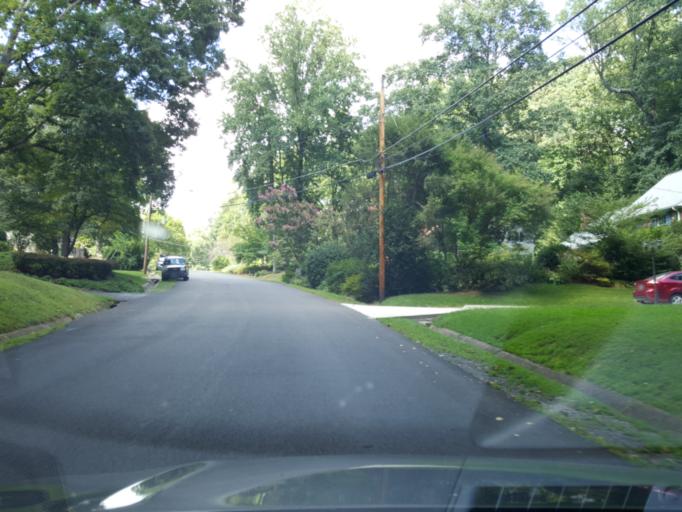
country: US
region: Virginia
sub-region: Fairfax County
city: Annandale
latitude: 38.8133
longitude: -77.1819
